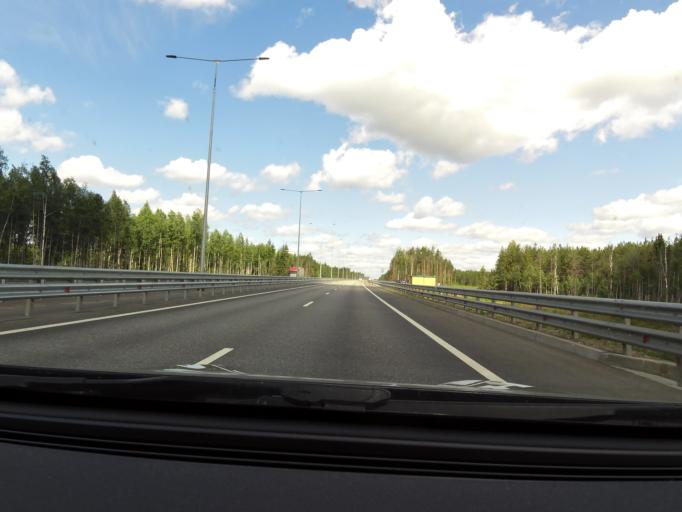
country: RU
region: Tverskaya
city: Krasnomayskiy
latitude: 57.6384
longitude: 34.2362
